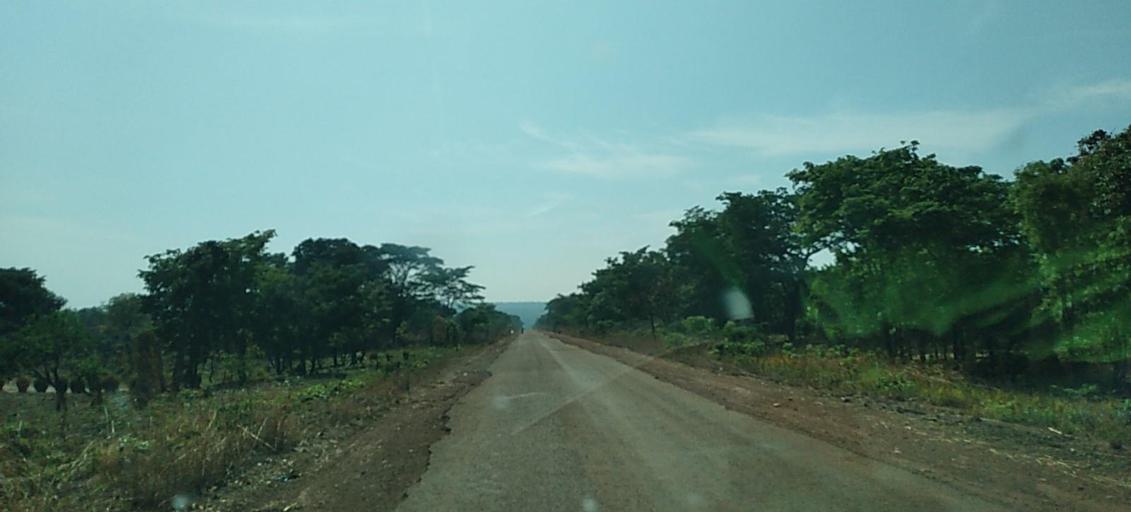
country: ZM
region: North-Western
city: Mwinilunga
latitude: -11.8221
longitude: 25.1056
